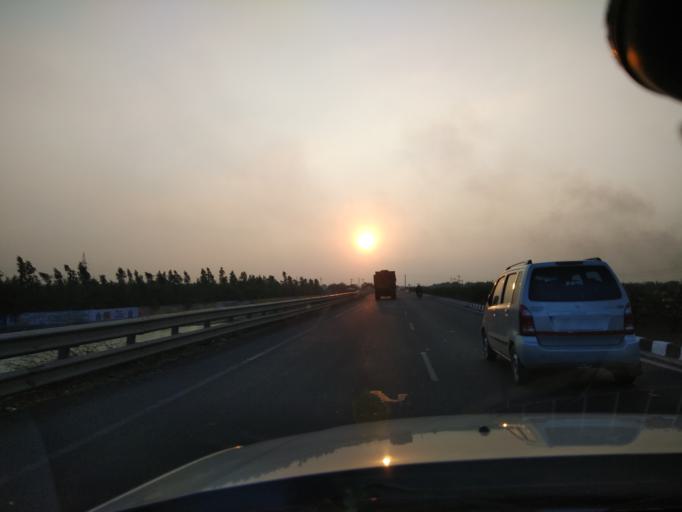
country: IN
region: Gujarat
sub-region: Jamnagar
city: Bedi
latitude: 22.4451
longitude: 70.0025
